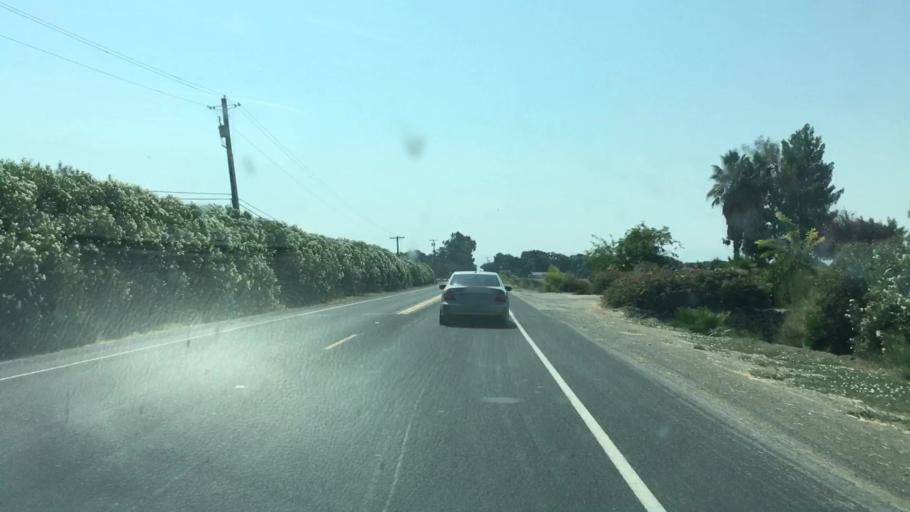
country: US
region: California
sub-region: San Joaquin County
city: Tracy
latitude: 37.8108
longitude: -121.4497
